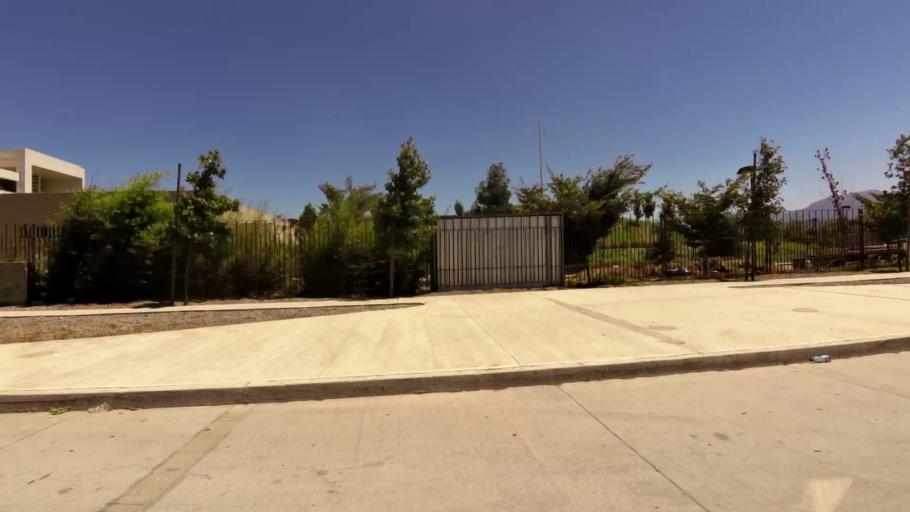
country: CL
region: O'Higgins
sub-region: Provincia de Cachapoal
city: Rancagua
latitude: -34.1537
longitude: -70.7650
